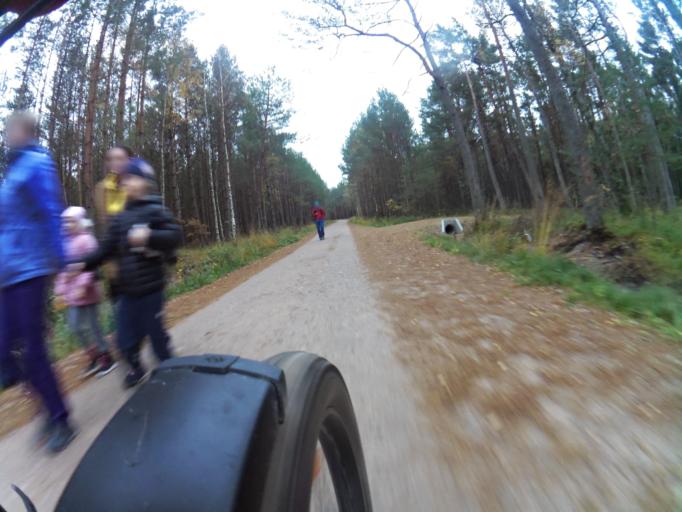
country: PL
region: Pomeranian Voivodeship
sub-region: Powiat wejherowski
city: Choczewo
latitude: 54.7823
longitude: 17.7335
